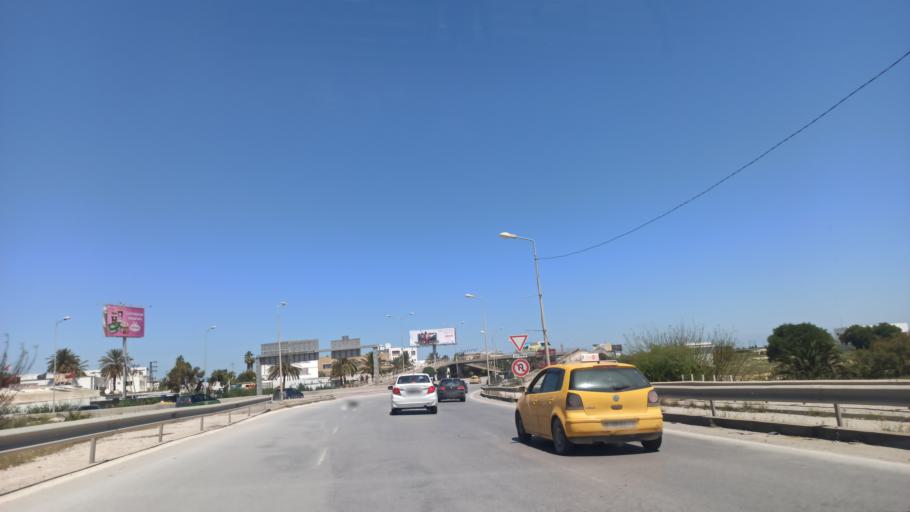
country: TN
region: Ariana
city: Ariana
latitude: 36.8269
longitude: 10.2033
